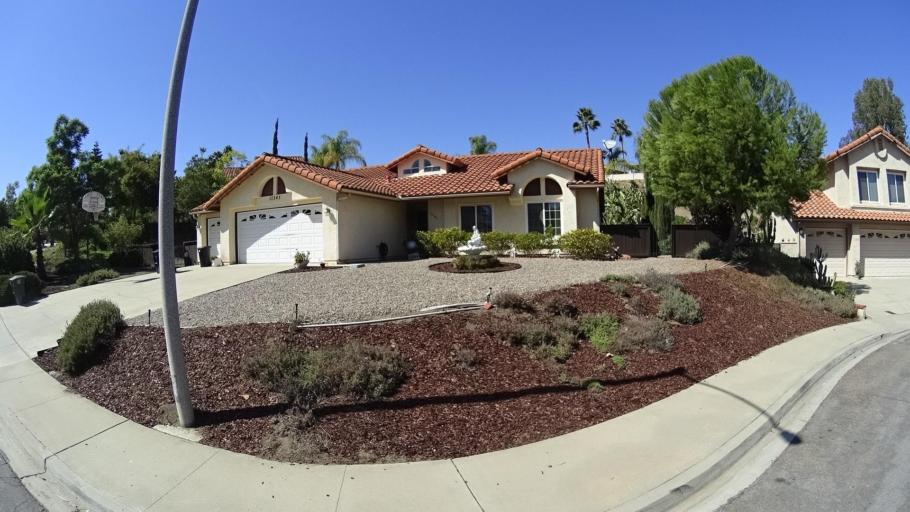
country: US
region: California
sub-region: San Diego County
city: Rancho San Diego
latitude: 32.7571
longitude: -116.9370
